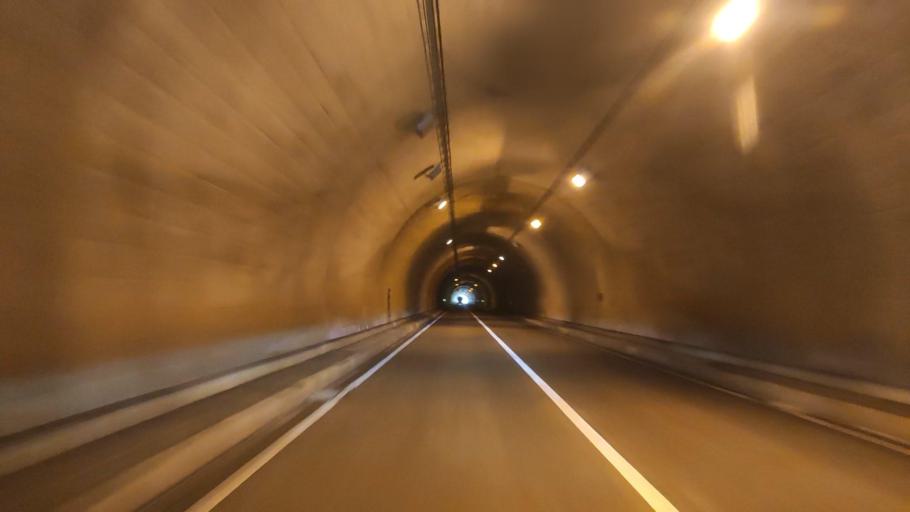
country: JP
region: Wakayama
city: Shingu
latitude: 33.9210
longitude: 135.9095
